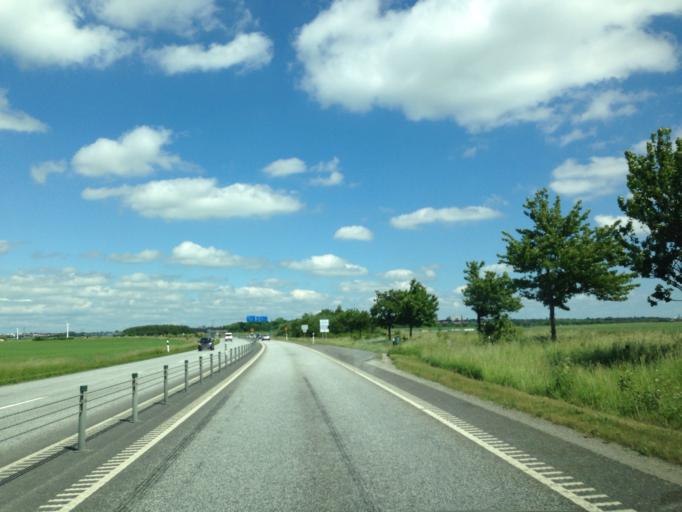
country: SE
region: Skane
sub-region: Staffanstorps Kommun
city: Hjaerup
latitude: 55.6930
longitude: 13.1287
